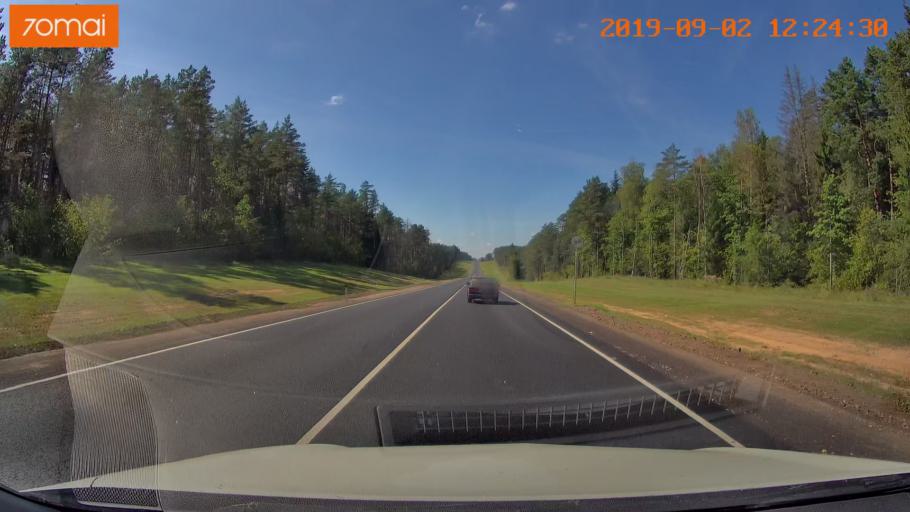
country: RU
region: Smolensk
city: Shumyachi
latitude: 53.8678
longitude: 32.6069
